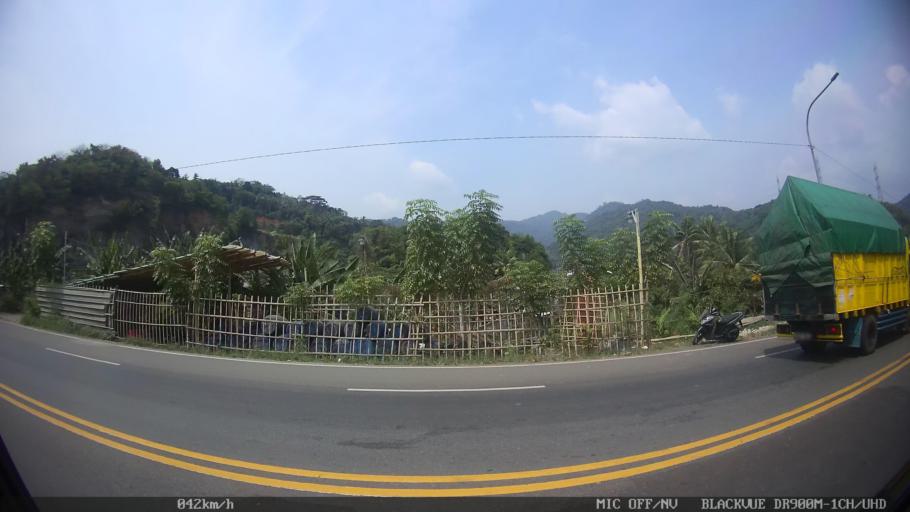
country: ID
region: Banten
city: Curug
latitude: -5.9544
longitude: 106.0023
